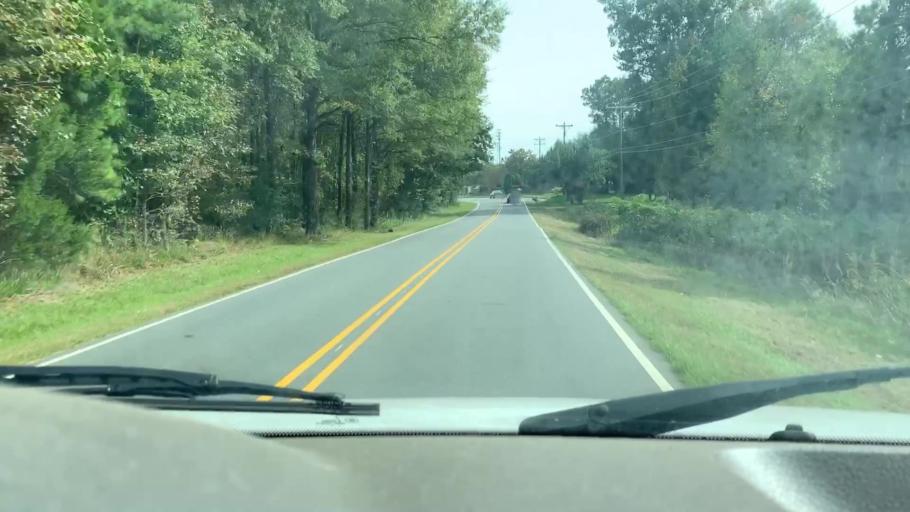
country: US
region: North Carolina
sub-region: Mecklenburg County
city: Huntersville
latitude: 35.4240
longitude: -80.7594
